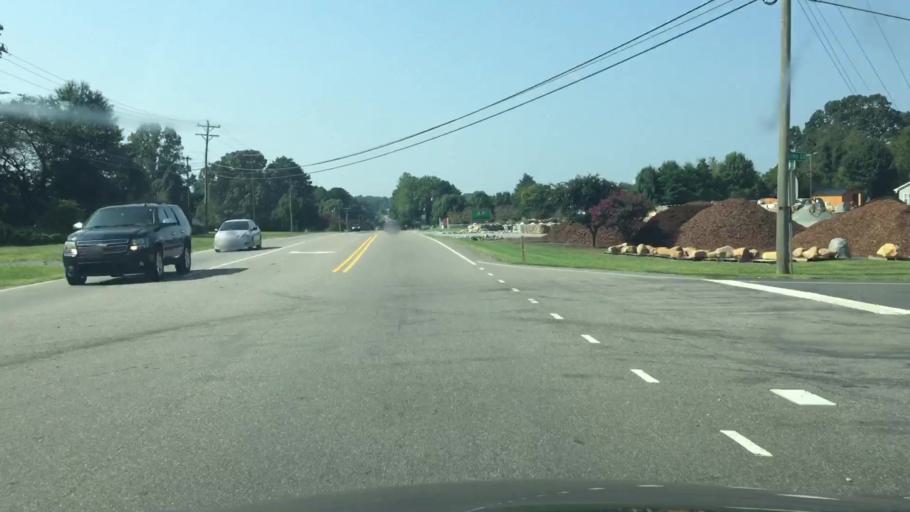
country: US
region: North Carolina
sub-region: Iredell County
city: Mooresville
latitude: 35.5770
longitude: -80.8414
